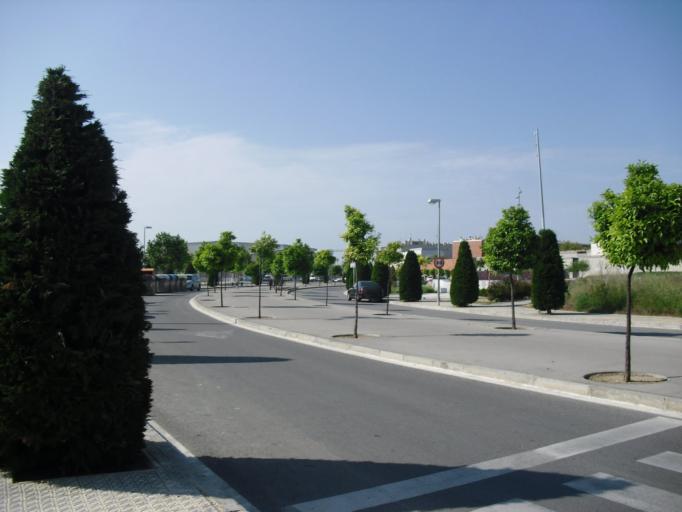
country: ES
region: Catalonia
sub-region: Provincia de Barcelona
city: Vilanova i la Geltru
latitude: 41.2337
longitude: 1.7300
